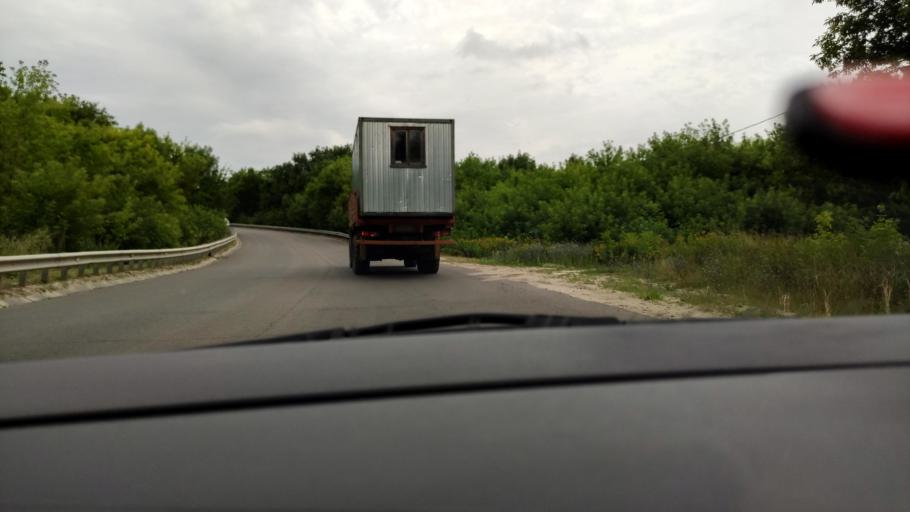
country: RU
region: Voronezj
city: Ramon'
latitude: 51.9043
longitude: 39.3368
